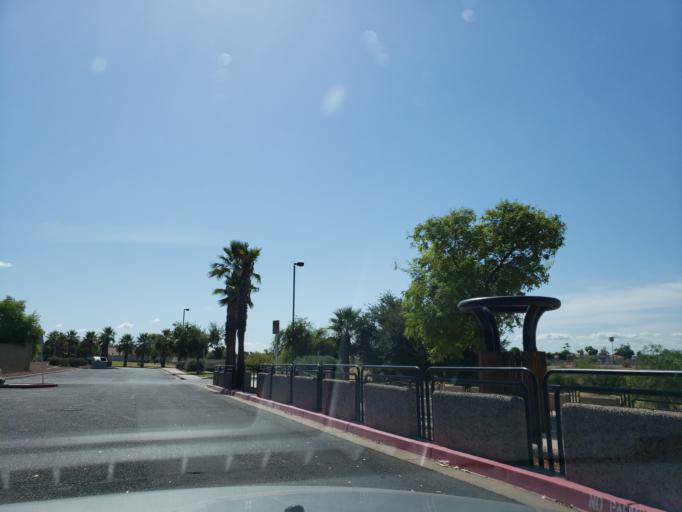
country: US
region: Arizona
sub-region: Maricopa County
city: Peoria
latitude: 33.6233
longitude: -112.2045
